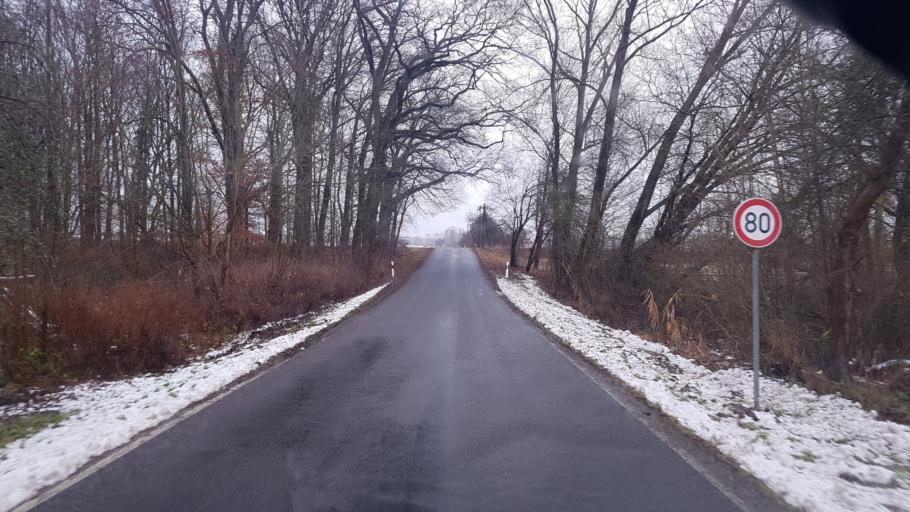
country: DE
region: Brandenburg
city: Lieberose
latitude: 51.9812
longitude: 14.3135
